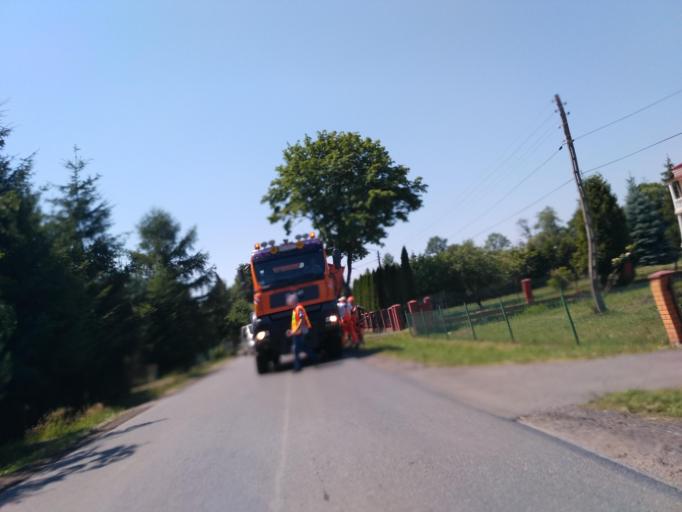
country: PL
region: Subcarpathian Voivodeship
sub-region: Powiat sanocki
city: Niebieszczany
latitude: 49.5396
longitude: 22.1311
